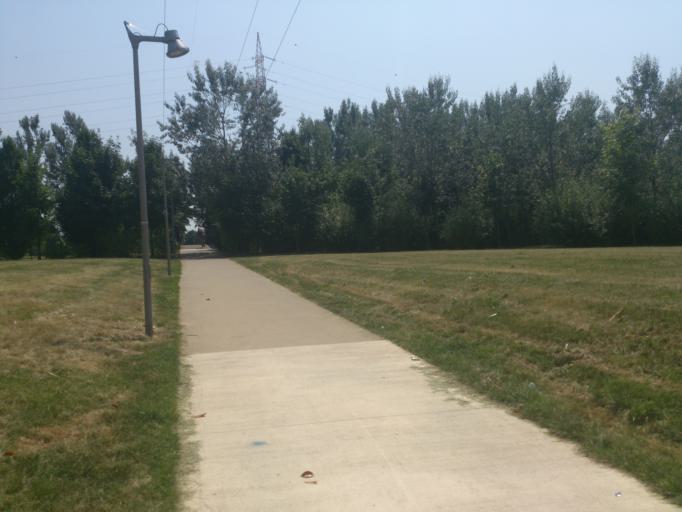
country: IT
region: Lombardy
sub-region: Citta metropolitana di Milano
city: Cologno Monzese
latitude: 45.5189
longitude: 9.2744
